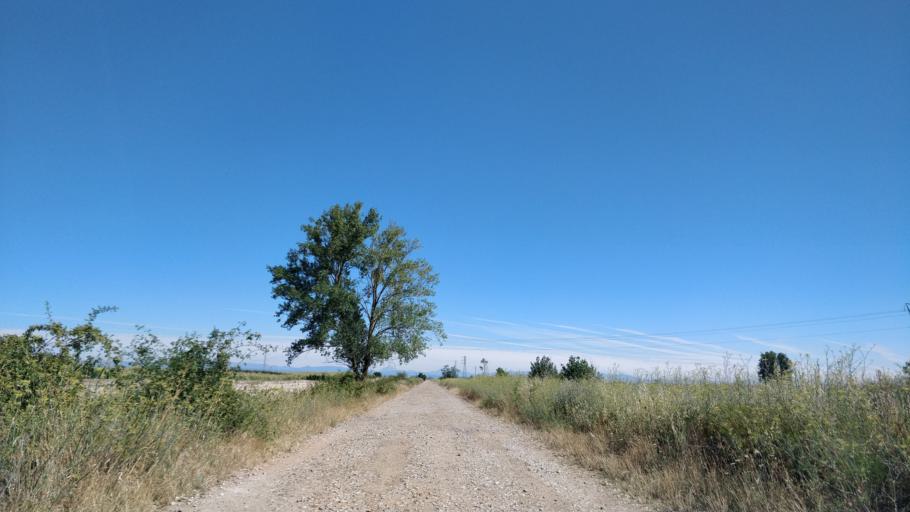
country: ES
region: Castille and Leon
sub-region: Provincia de Leon
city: Bustillo del Paramo
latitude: 42.4243
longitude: -5.8210
